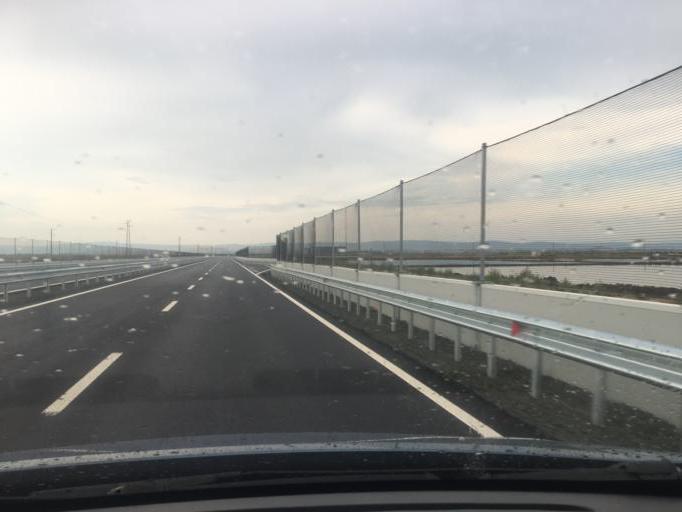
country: BG
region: Burgas
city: Aheloy
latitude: 42.6141
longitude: 27.6238
